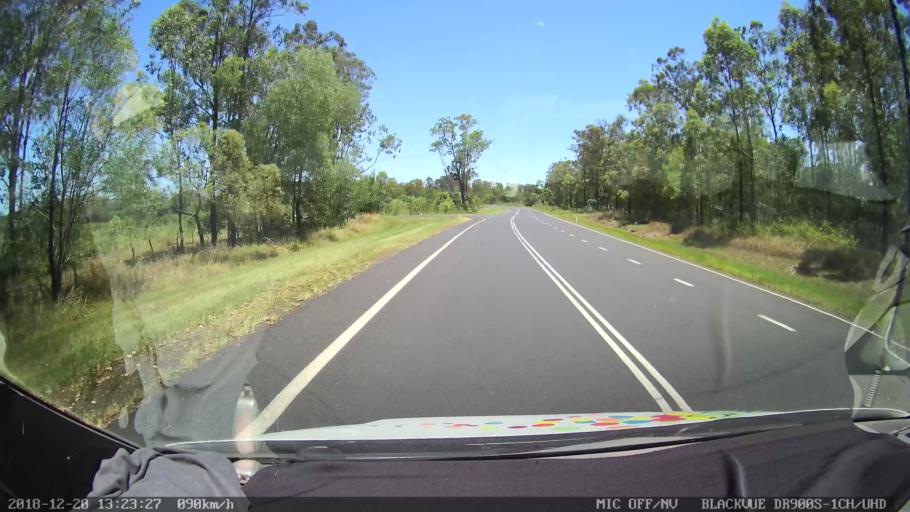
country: AU
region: New South Wales
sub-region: Richmond Valley
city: Casino
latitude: -29.1048
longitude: 152.9998
